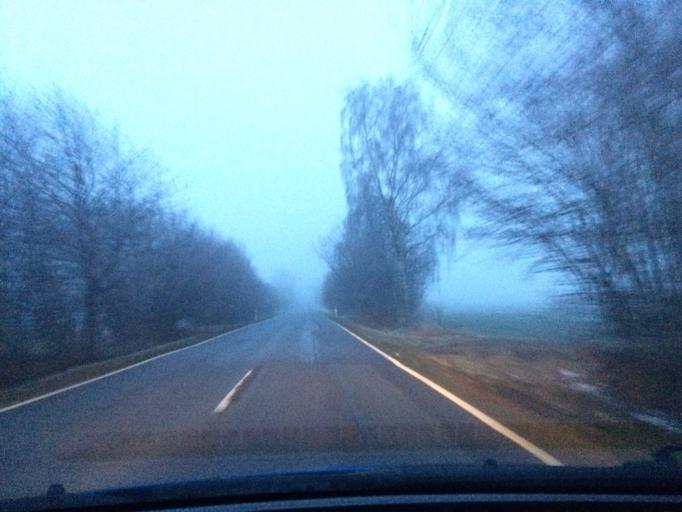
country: DE
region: Schleswig-Holstein
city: Wiershop
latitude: 53.4498
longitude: 10.4531
